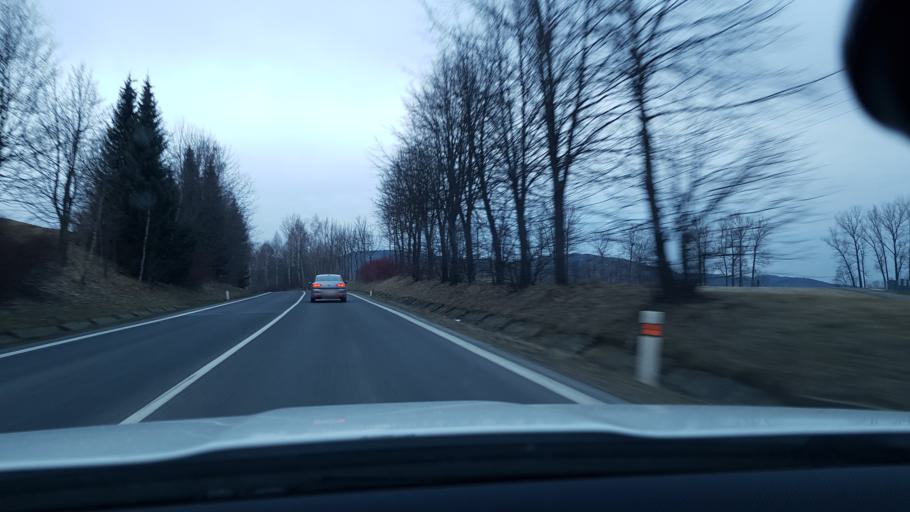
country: CZ
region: Olomoucky
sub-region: Okres Jesenik
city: Jesenik
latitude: 50.2163
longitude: 17.1999
